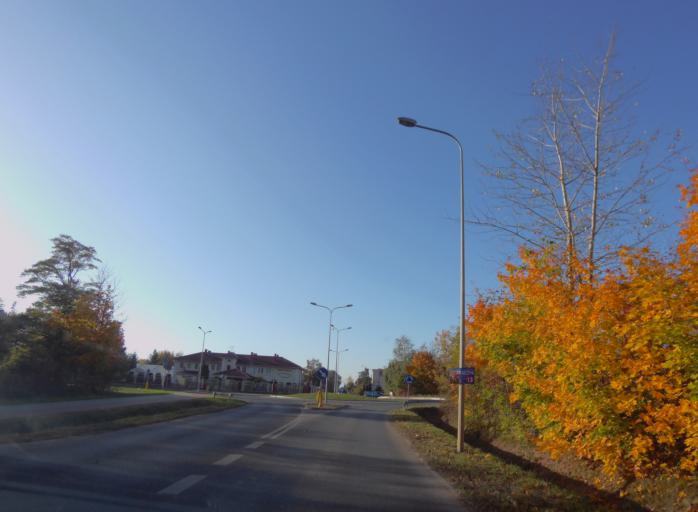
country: PL
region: Masovian Voivodeship
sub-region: Powiat pruszkowski
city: Otrebusy
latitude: 52.1550
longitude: 20.7643
